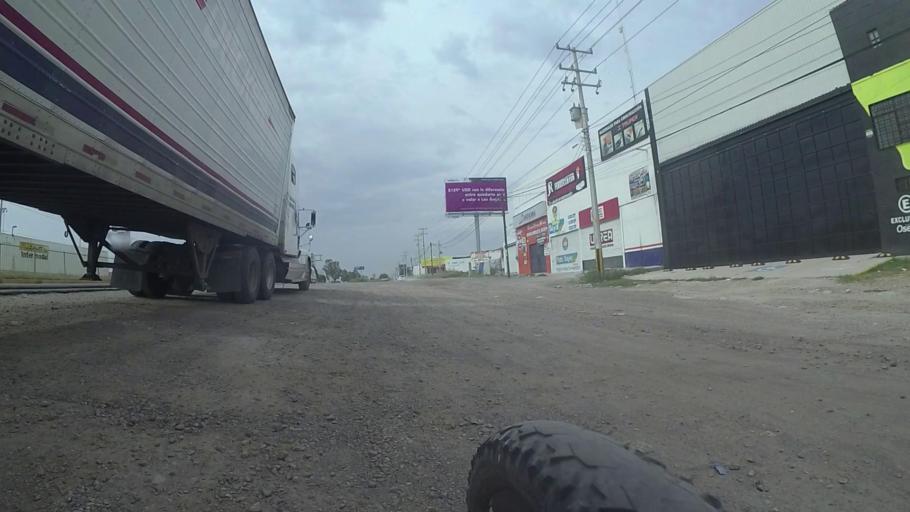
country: MX
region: Aguascalientes
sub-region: Aguascalientes
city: Penuelas (El Cienegal)
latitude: 21.7291
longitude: -102.2766
